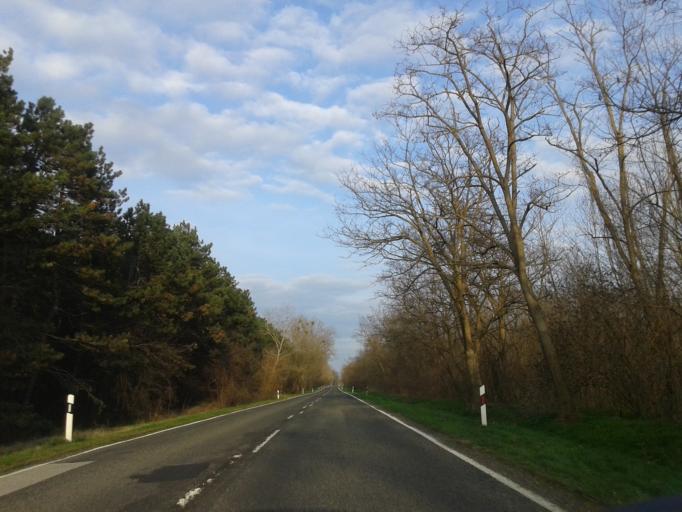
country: HU
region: Gyor-Moson-Sopron
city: Bony
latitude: 47.7324
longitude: 17.8764
